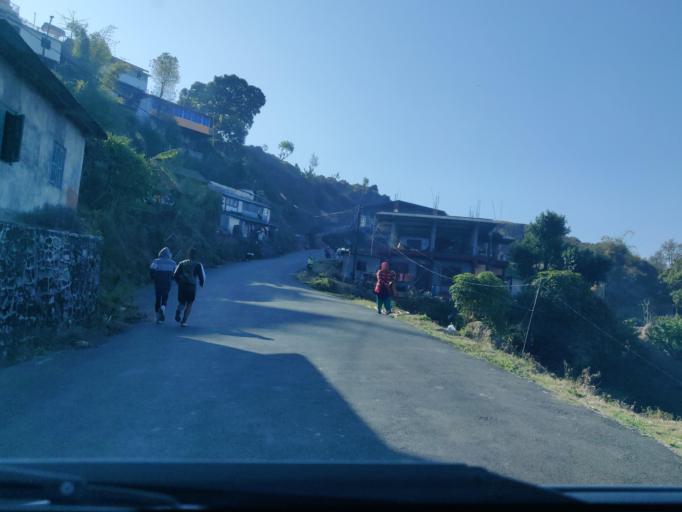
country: NP
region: Western Region
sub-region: Gandaki Zone
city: Pokhara
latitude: 28.2357
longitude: 83.9664
